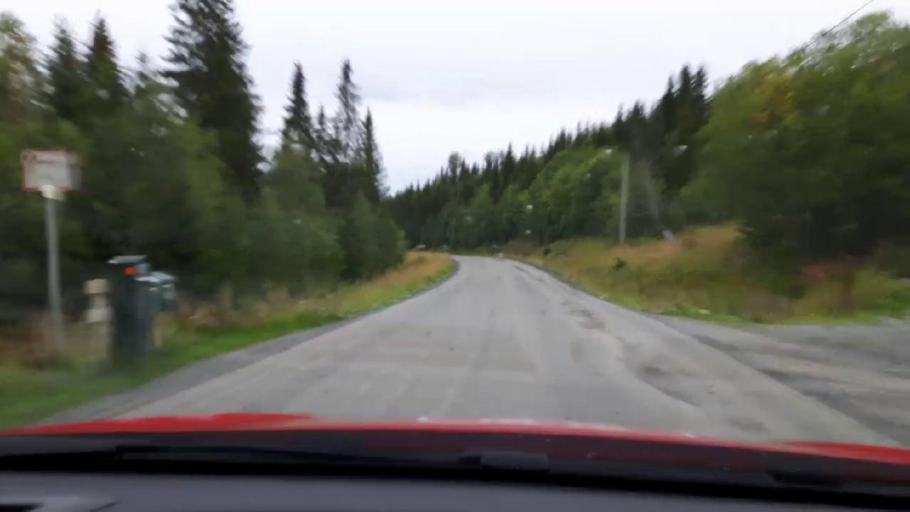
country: SE
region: Jaemtland
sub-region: Are Kommun
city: Jarpen
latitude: 63.4172
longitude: 13.3530
